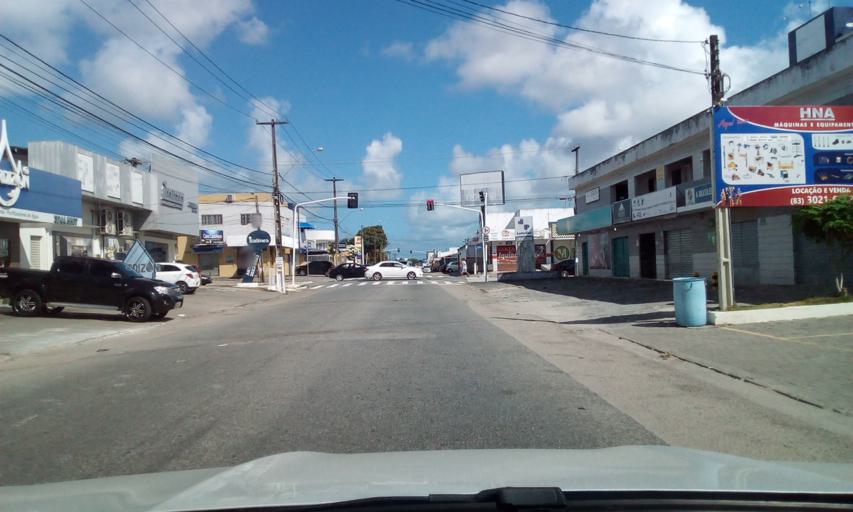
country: BR
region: Paraiba
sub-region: Joao Pessoa
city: Joao Pessoa
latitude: -7.1222
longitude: -34.8631
